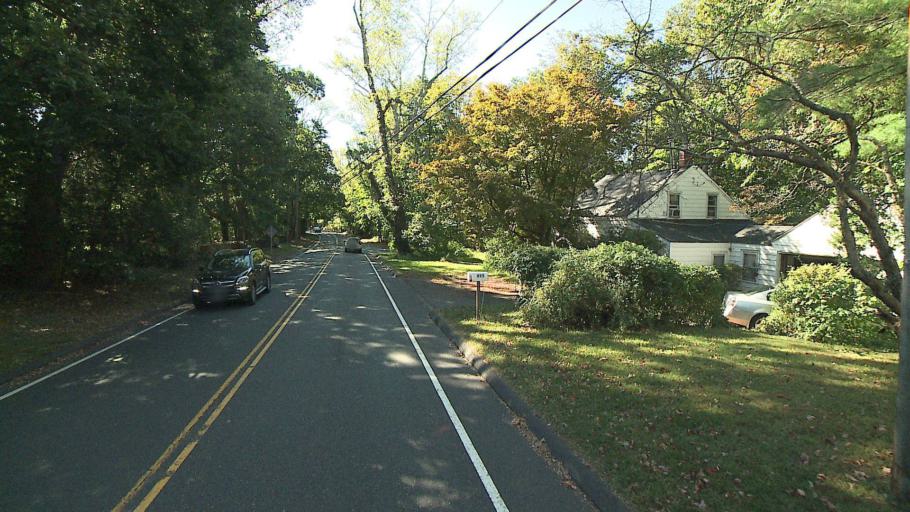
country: US
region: Connecticut
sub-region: Fairfield County
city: New Canaan
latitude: 41.1145
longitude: -73.4858
